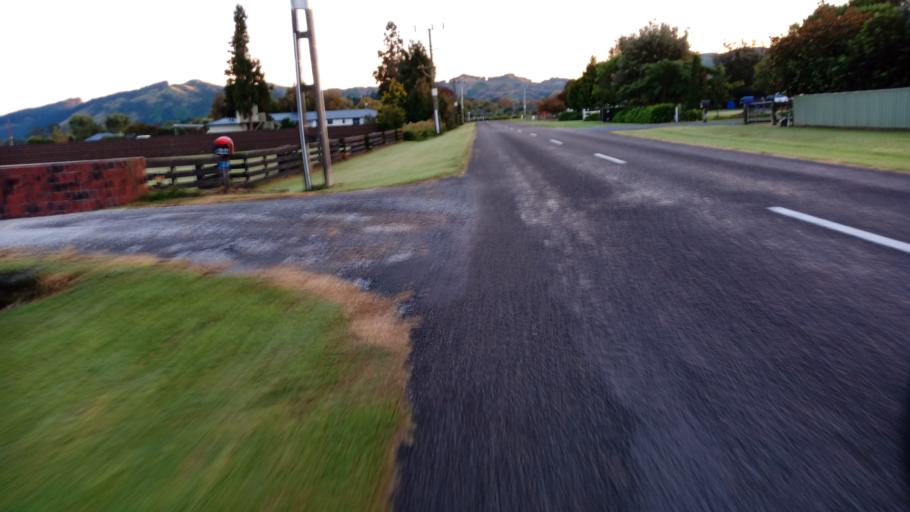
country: NZ
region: Gisborne
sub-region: Gisborne District
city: Gisborne
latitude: -38.6352
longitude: 177.9862
